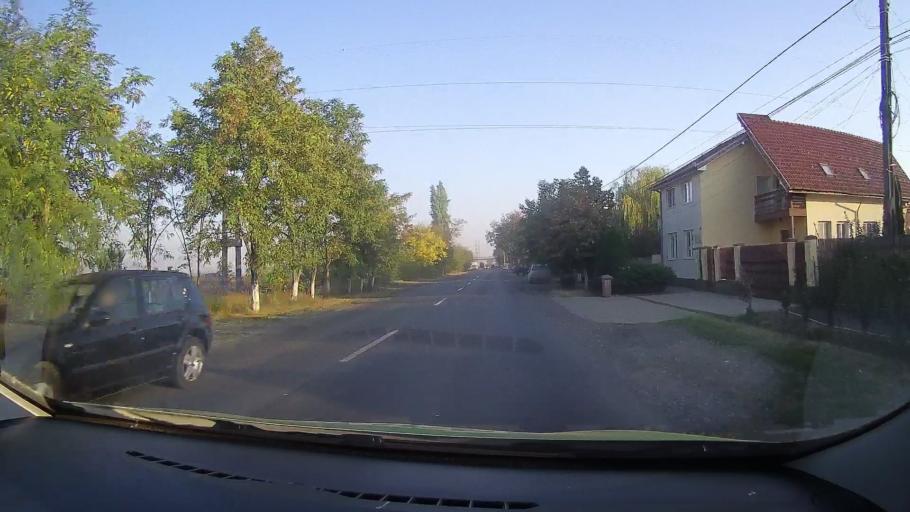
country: RO
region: Arad
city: Arad
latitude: 46.2135
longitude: 21.3206
